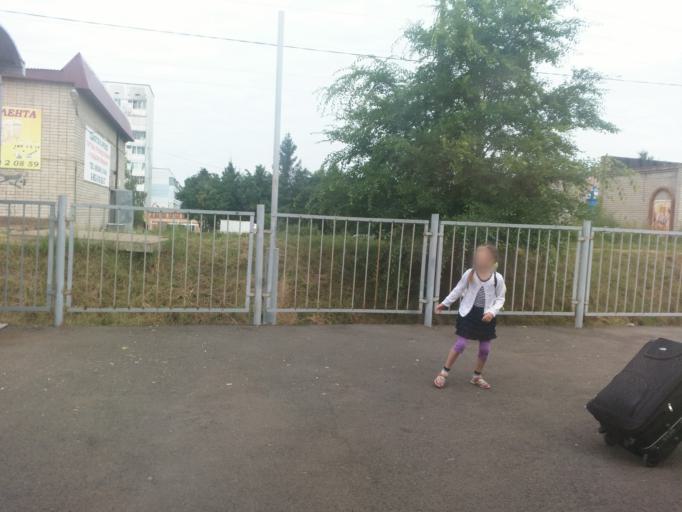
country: RU
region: Tatarstan
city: Mendeleyevsk
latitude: 55.8860
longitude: 52.3129
